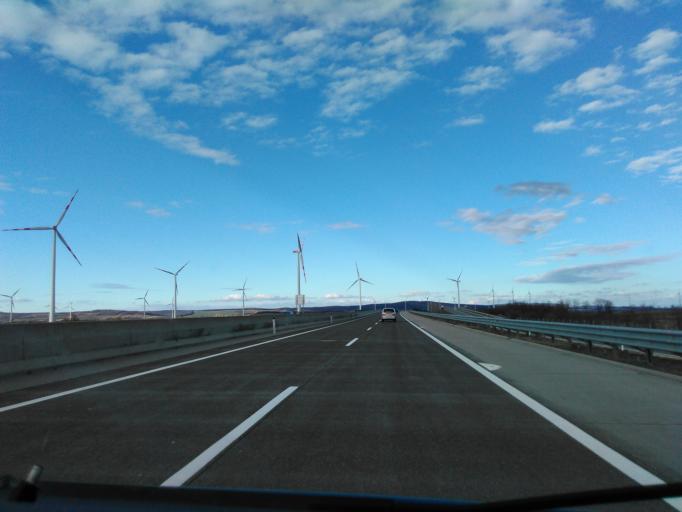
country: AT
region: Burgenland
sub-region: Politischer Bezirk Neusiedl am See
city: Gattendorf
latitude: 48.0472
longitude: 16.9941
